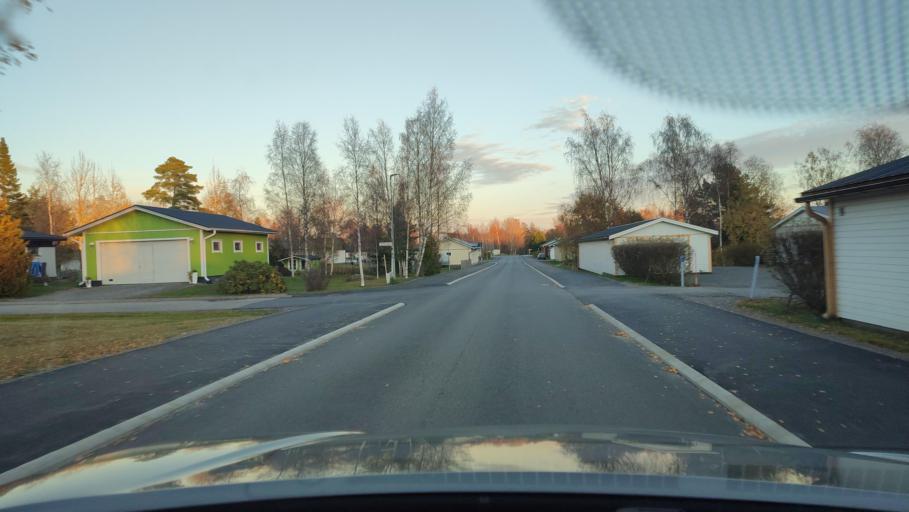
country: FI
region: Ostrobothnia
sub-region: Sydosterbotten
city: Kristinestad
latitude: 62.2817
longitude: 21.3592
